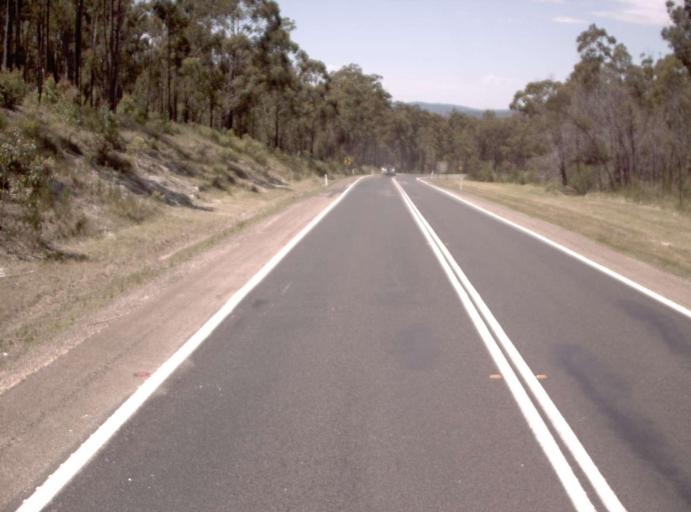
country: AU
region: New South Wales
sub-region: Bombala
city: Bombala
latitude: -37.5656
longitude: 149.1158
